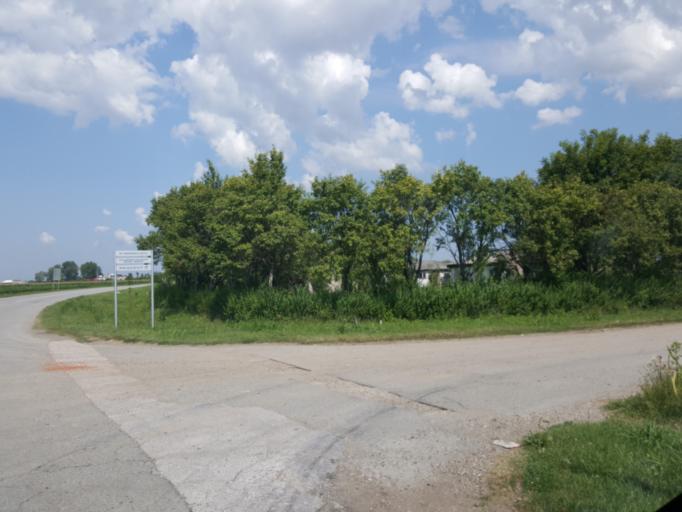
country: RS
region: Autonomna Pokrajina Vojvodina
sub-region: Sremski Okrug
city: Sremska Mitrovica
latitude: 44.9967
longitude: 19.6344
